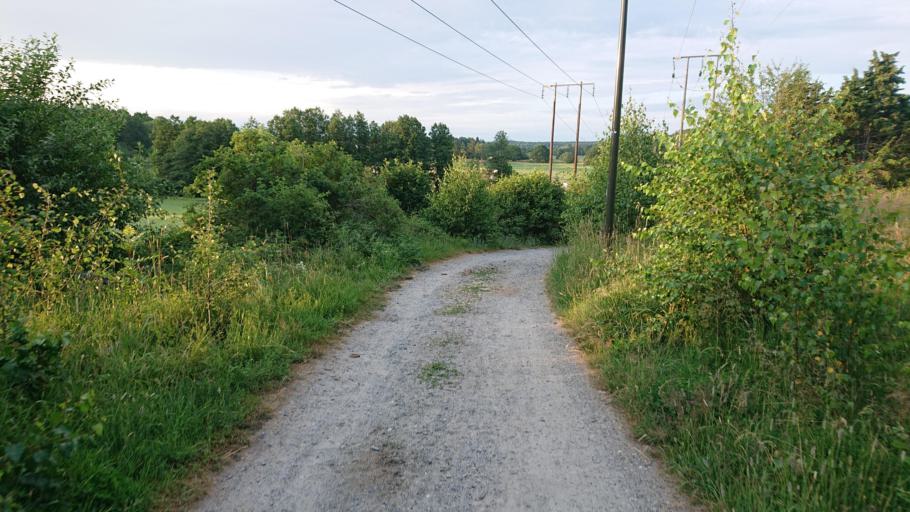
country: SE
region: Stockholm
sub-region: Osterakers Kommun
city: Akersberga
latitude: 59.4964
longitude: 18.2990
